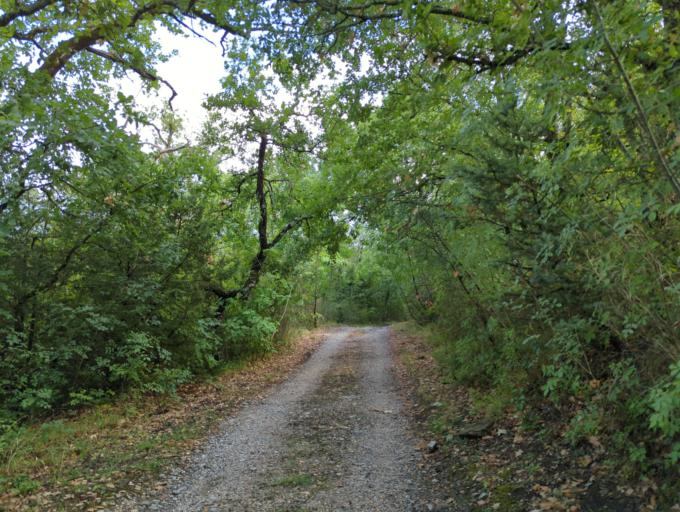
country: IT
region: Tuscany
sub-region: Province of Arezzo
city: Castiglion Fibocchi
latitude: 43.5437
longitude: 11.7673
